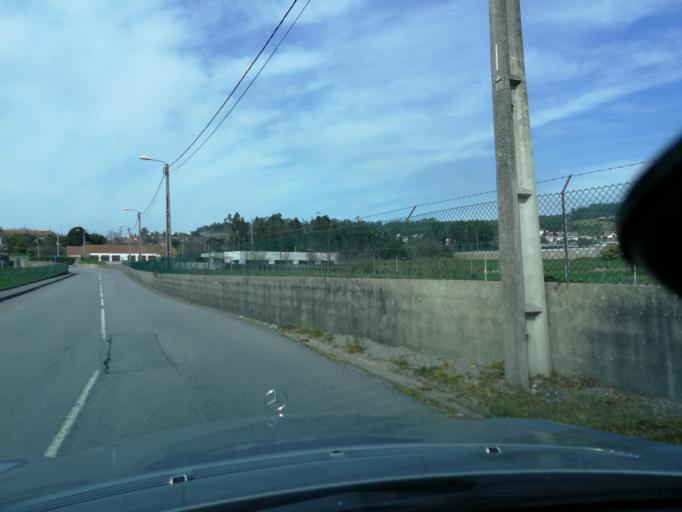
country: PT
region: Braga
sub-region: Vila Nova de Famalicao
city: Vila Nova de Famalicao
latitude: 41.4360
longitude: -8.5216
